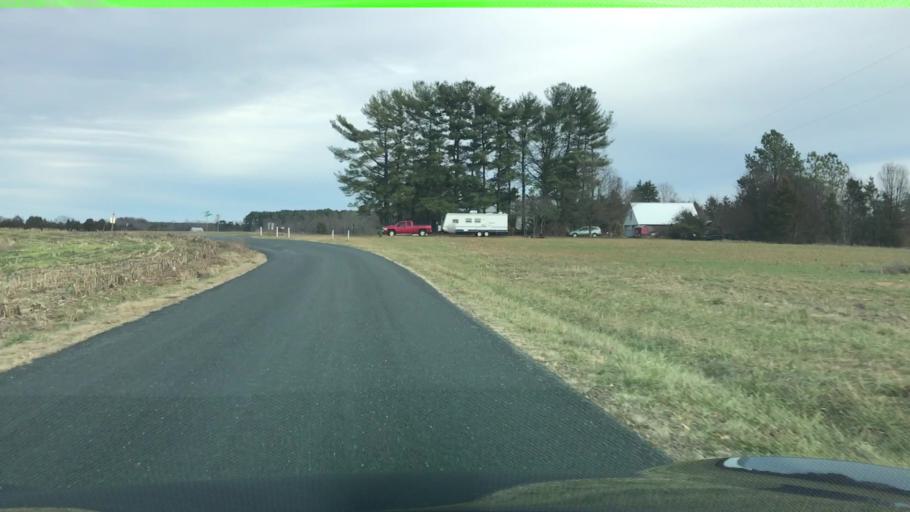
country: US
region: Virginia
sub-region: Appomattox County
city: Appomattox
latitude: 37.2464
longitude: -78.8818
